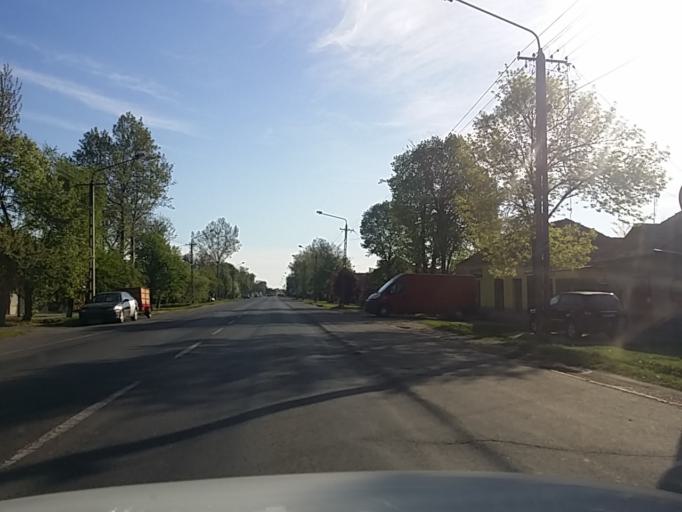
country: HU
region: Jasz-Nagykun-Szolnok
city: Torokszentmiklos
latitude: 47.1752
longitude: 20.3841
